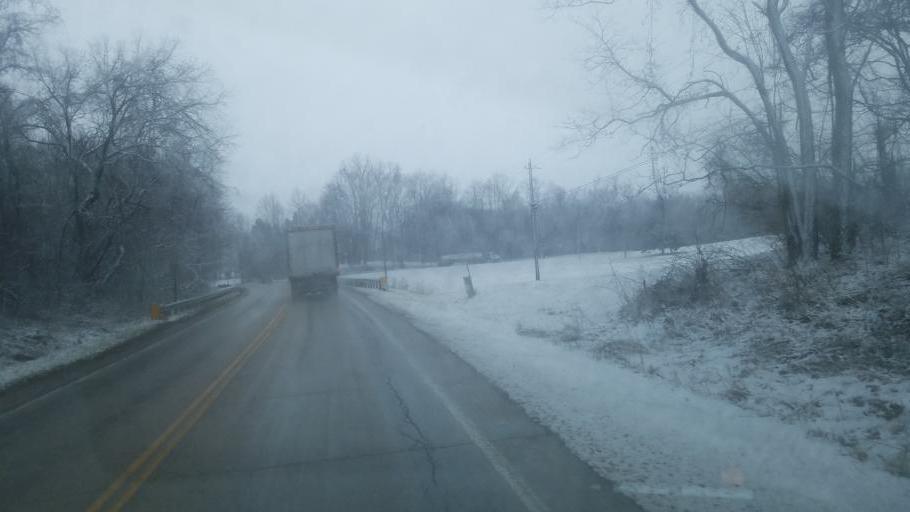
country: US
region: Ohio
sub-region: Portage County
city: Garrettsville
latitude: 41.3173
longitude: -81.0949
